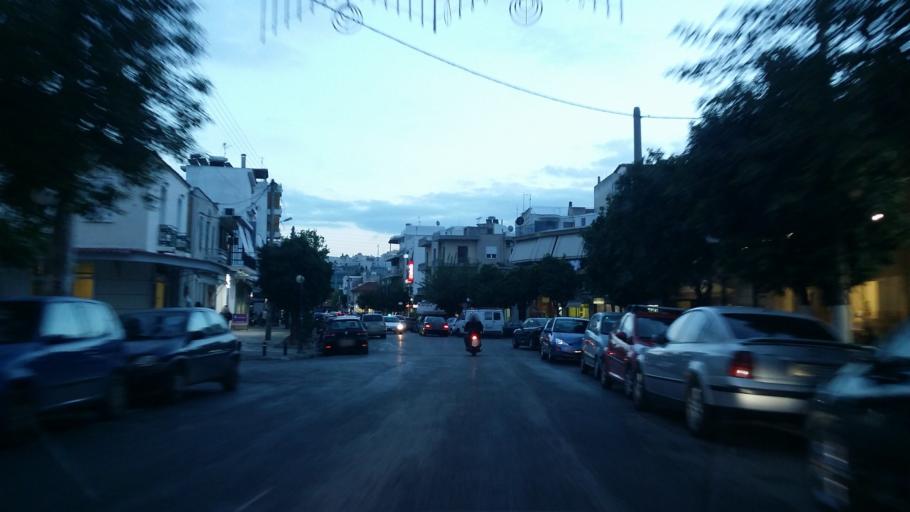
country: GR
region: Attica
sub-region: Nomarchia Athinas
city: Nea Ionia
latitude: 38.0431
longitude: 23.7512
